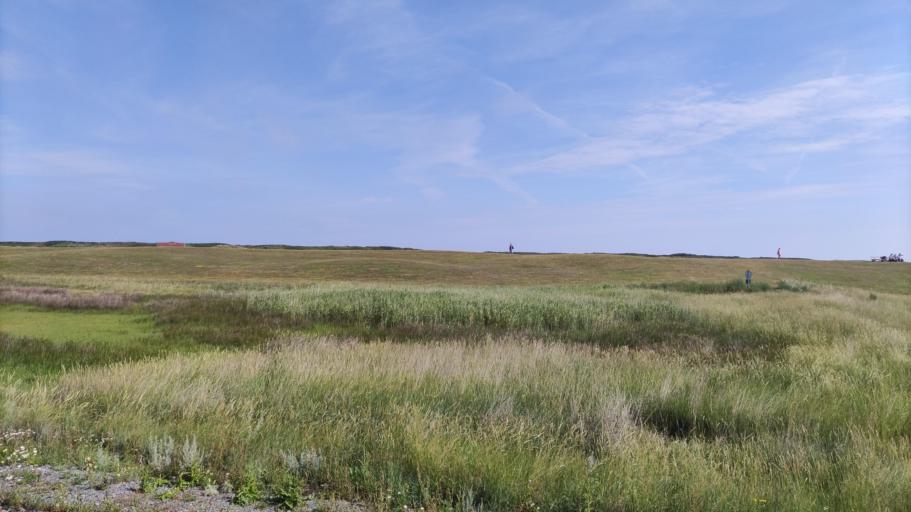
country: DE
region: Lower Saxony
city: Wangerooge
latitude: 53.7894
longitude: 7.8772
